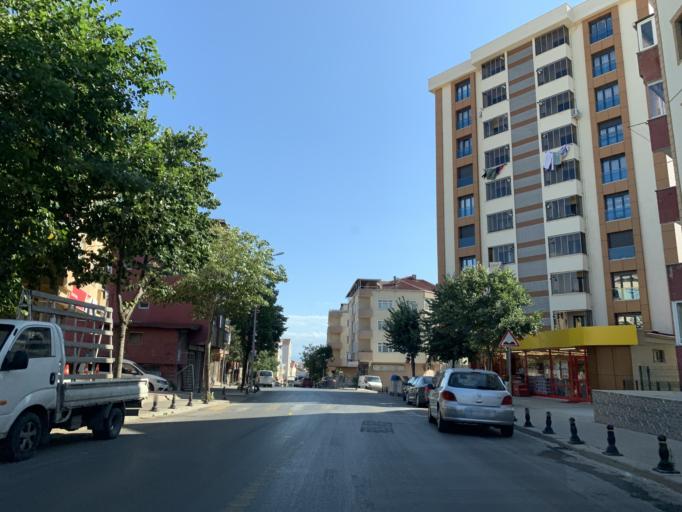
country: TR
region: Istanbul
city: Pendik
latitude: 40.8772
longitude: 29.2807
